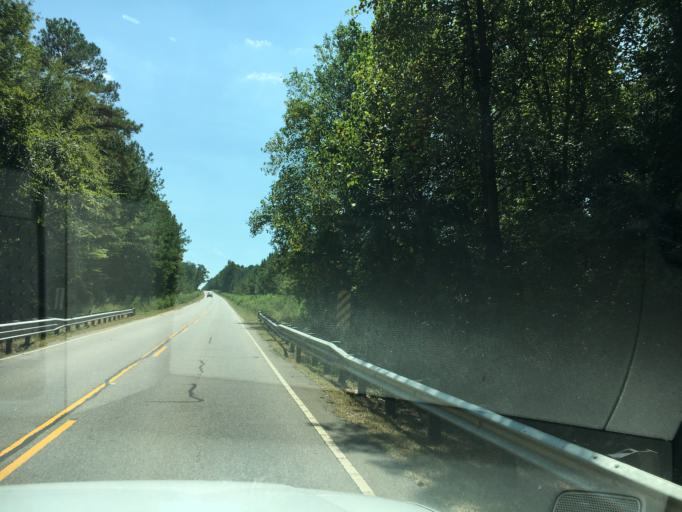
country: US
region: South Carolina
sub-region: Edgefield County
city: Johnston
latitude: 33.8728
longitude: -81.6925
